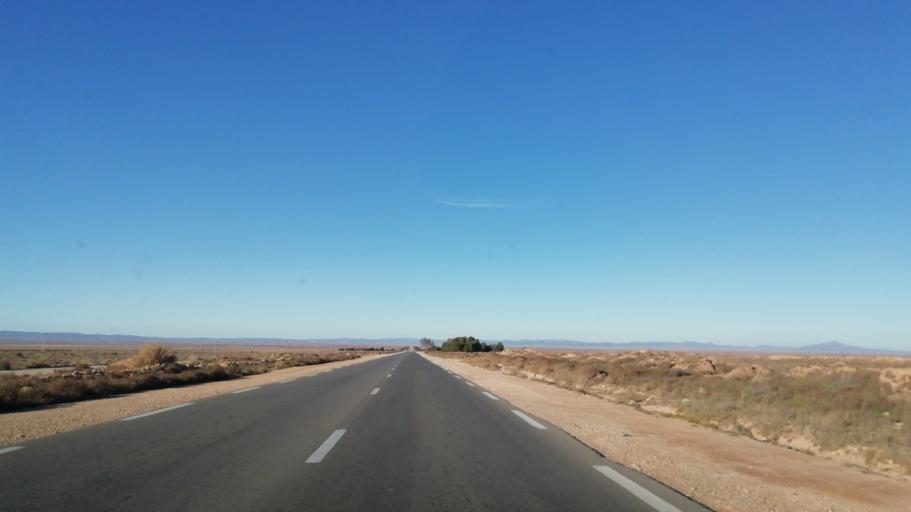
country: DZ
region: Tlemcen
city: Sebdou
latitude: 34.3115
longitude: -1.2623
